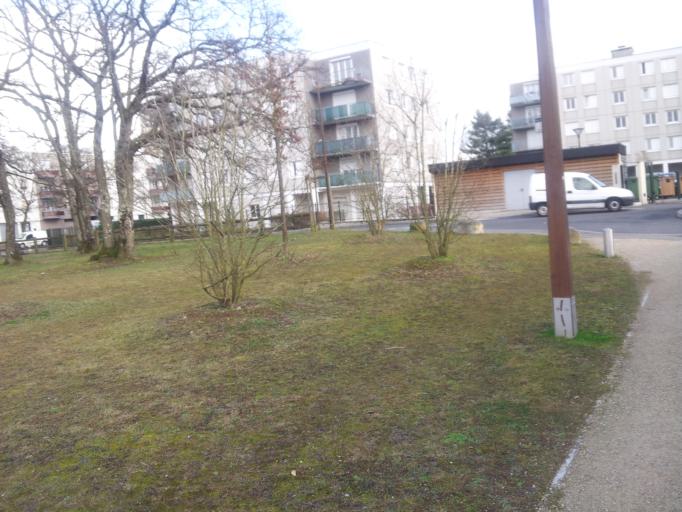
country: FR
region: Centre
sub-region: Departement du Loiret
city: Saint-Cyr-en-Val
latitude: 47.8350
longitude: 1.9296
